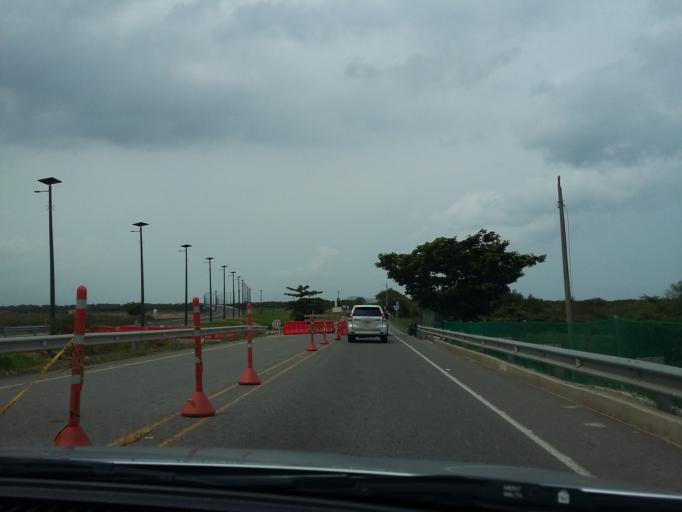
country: CO
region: Bolivar
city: Cartagena
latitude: 10.4976
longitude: -75.4779
